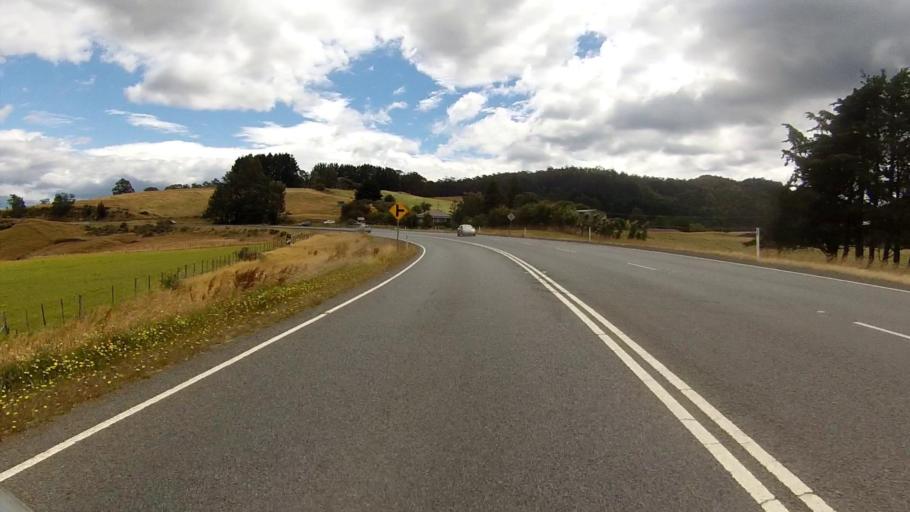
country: AU
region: Tasmania
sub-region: Kingborough
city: Margate
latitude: -42.9774
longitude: 147.1592
